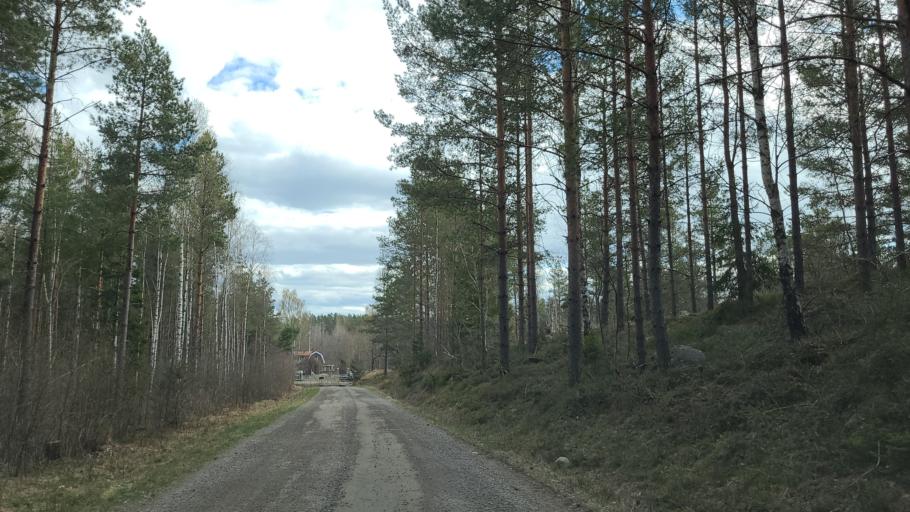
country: SE
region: OEstergoetland
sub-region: Norrkopings Kommun
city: Krokek
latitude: 58.6819
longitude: 16.4251
